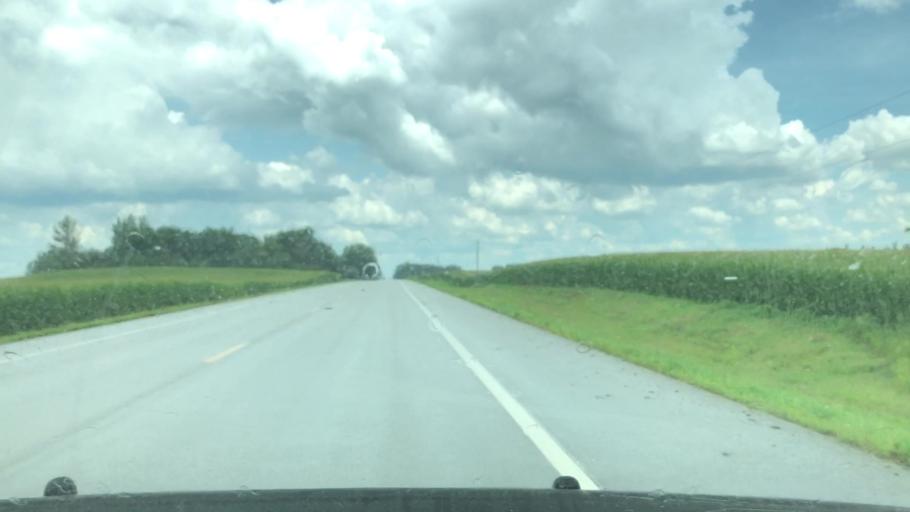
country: US
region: Minnesota
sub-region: Olmsted County
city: Stewartville
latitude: 43.9008
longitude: -92.5284
